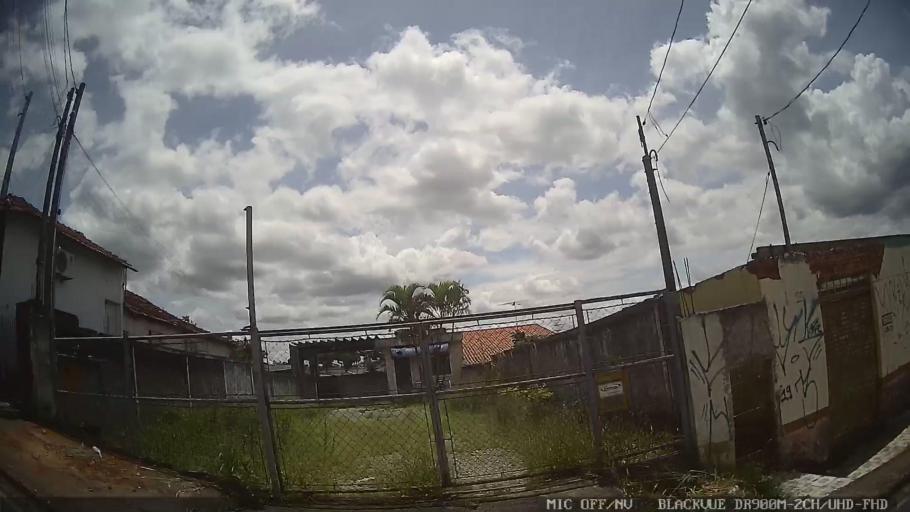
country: BR
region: Sao Paulo
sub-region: Mogi das Cruzes
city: Mogi das Cruzes
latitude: -23.5371
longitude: -46.2037
